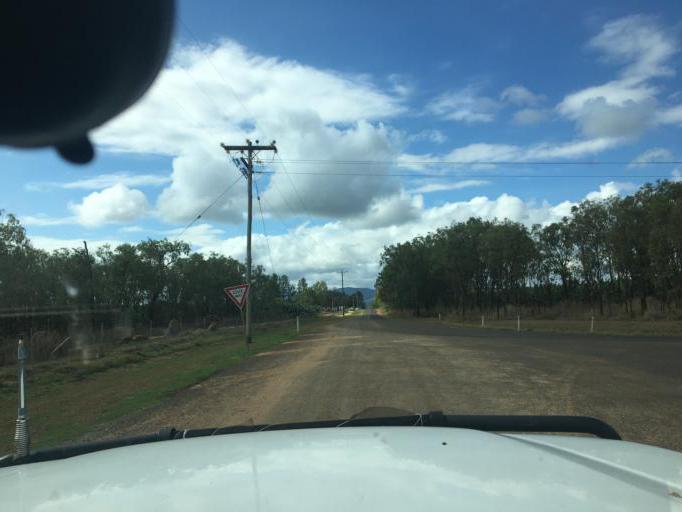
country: AU
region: Queensland
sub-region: Tablelands
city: Mareeba
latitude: -17.0988
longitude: 145.4118
